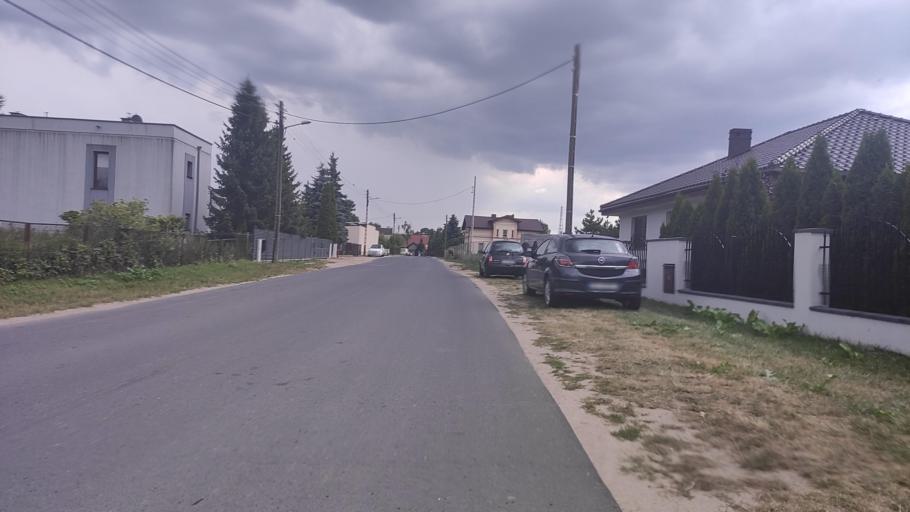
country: PL
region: Greater Poland Voivodeship
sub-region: Powiat poznanski
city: Swarzedz
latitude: 52.3886
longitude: 17.1172
